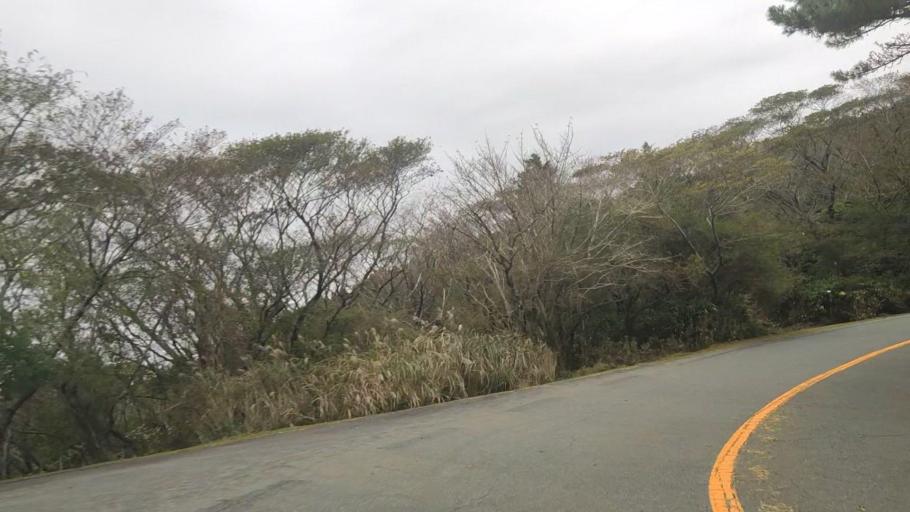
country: JP
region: Shizuoka
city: Heda
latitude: 34.9351
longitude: 138.8317
